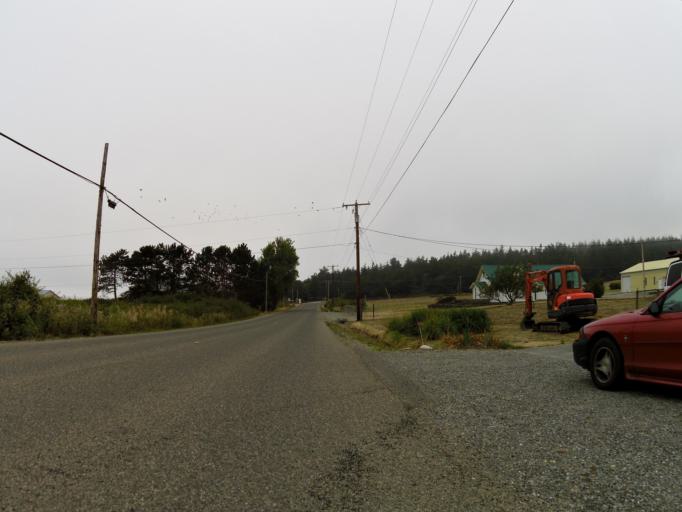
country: US
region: Washington
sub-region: Island County
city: Ault Field
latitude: 48.3055
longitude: -122.7129
